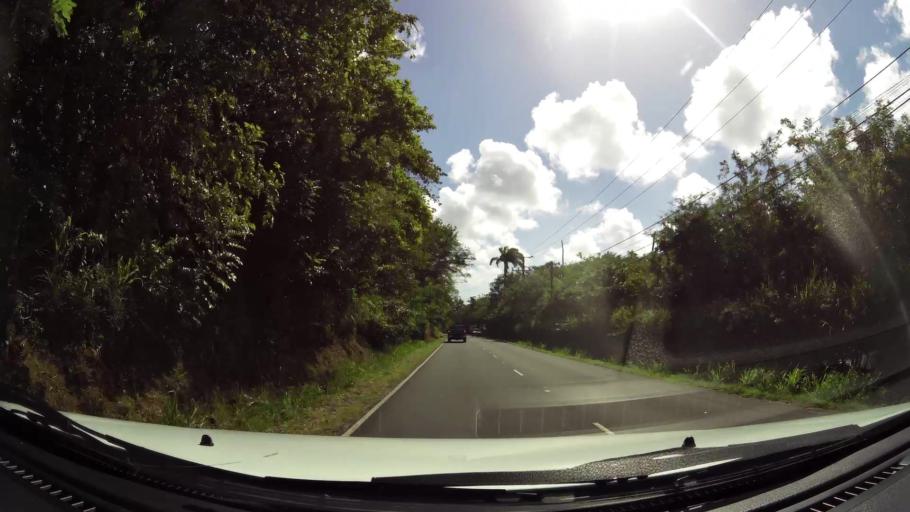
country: LC
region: Choiseul Quarter
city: Choiseul
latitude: 13.7598
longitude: -61.0265
